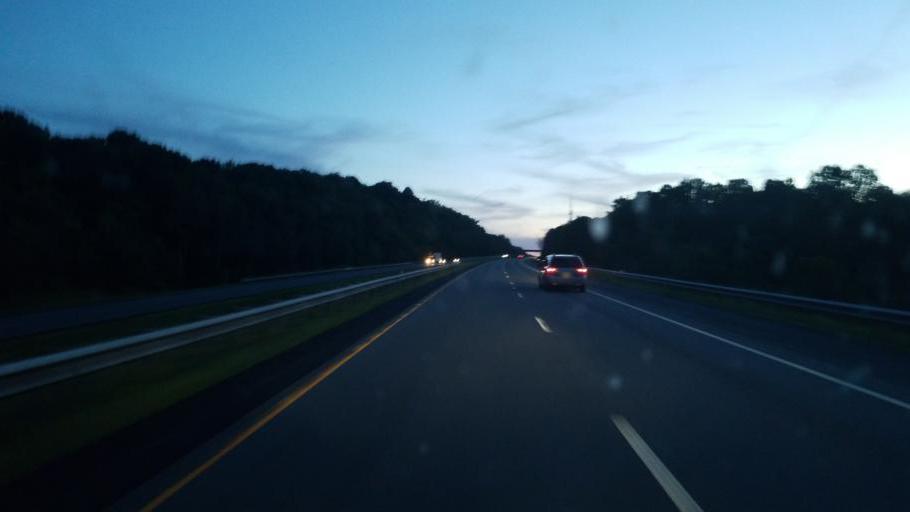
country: US
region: Ohio
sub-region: Summit County
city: Montrose-Ghent
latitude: 41.1966
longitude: -81.7014
